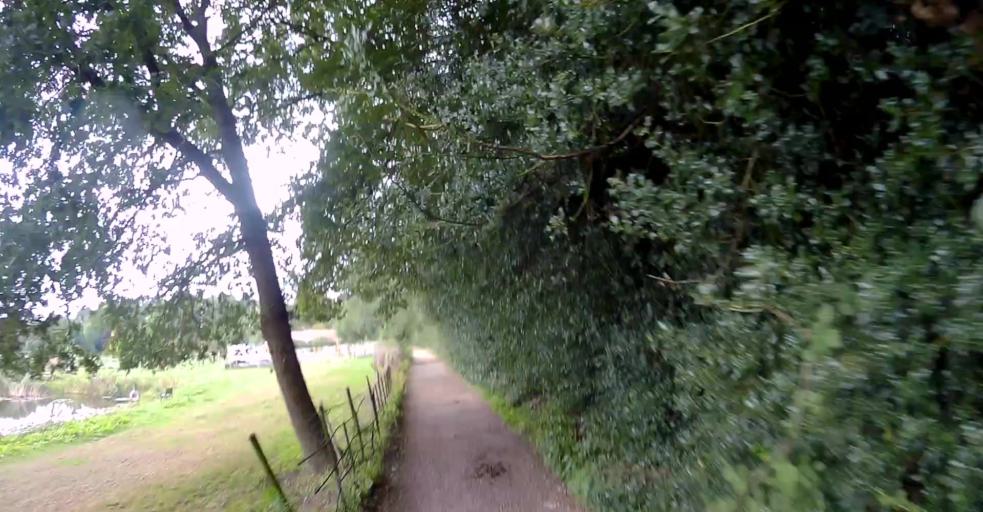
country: GB
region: England
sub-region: Surrey
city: Hale
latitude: 51.2163
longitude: -0.7703
